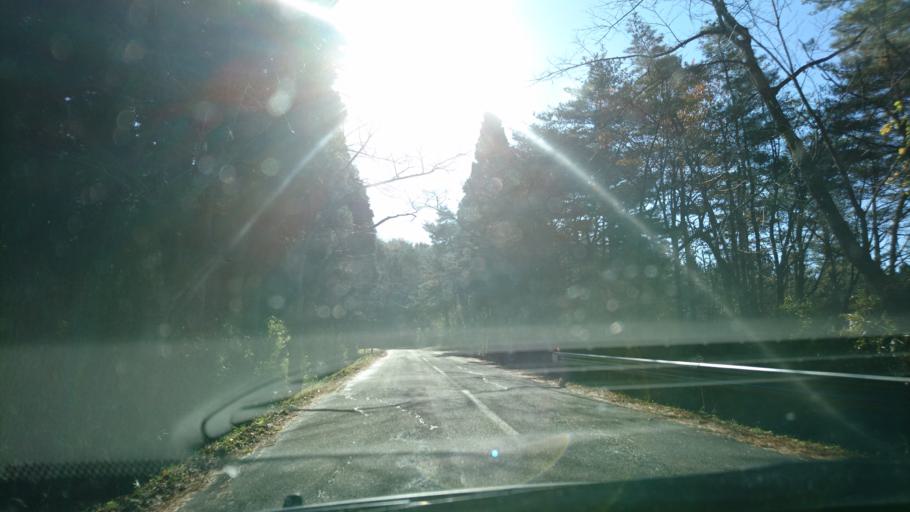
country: JP
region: Iwate
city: Ichinoseki
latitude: 38.9938
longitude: 141.0956
